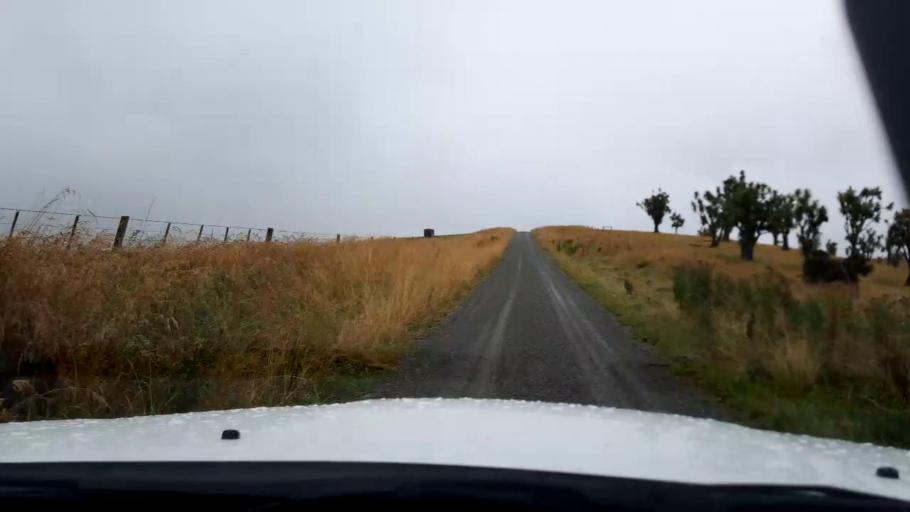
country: NZ
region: Canterbury
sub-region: Timaru District
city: Pleasant Point
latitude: -44.1744
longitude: 171.0928
